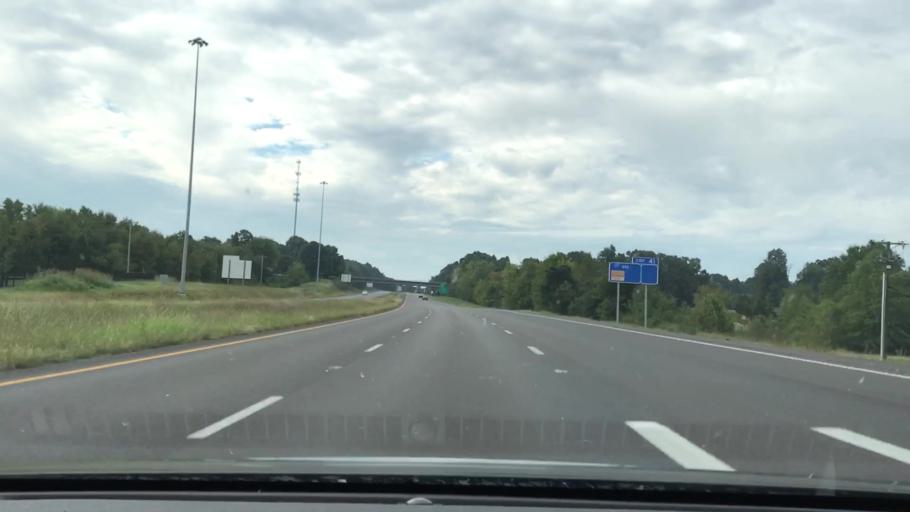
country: US
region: Kentucky
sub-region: Marshall County
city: Benton
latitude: 36.8653
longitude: -88.3667
